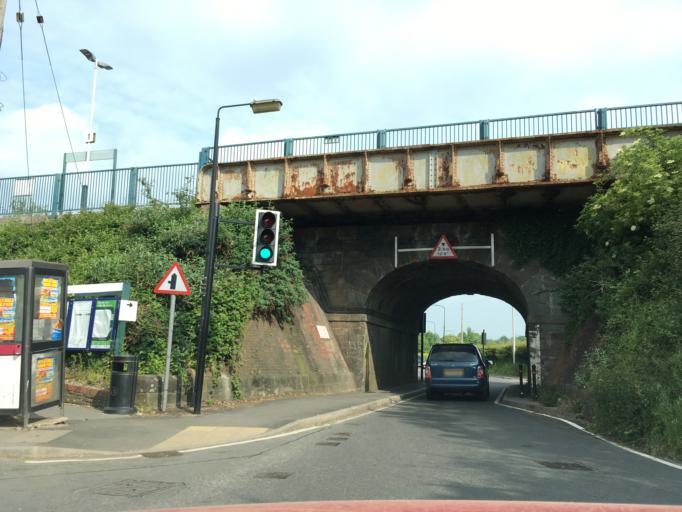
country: GB
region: England
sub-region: North Somerset
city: Nailsea
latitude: 51.4195
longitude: -2.7498
